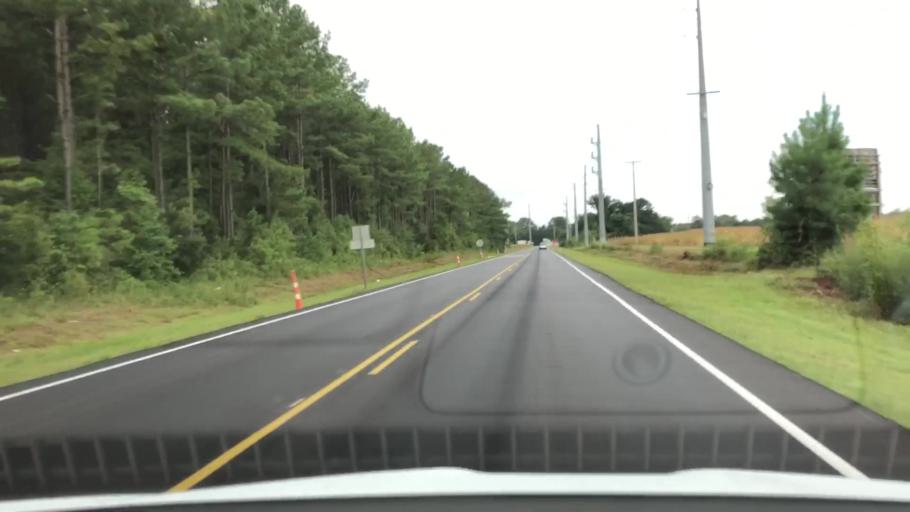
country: US
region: North Carolina
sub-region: Onslow County
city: Swansboro
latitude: 34.7877
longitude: -77.1227
